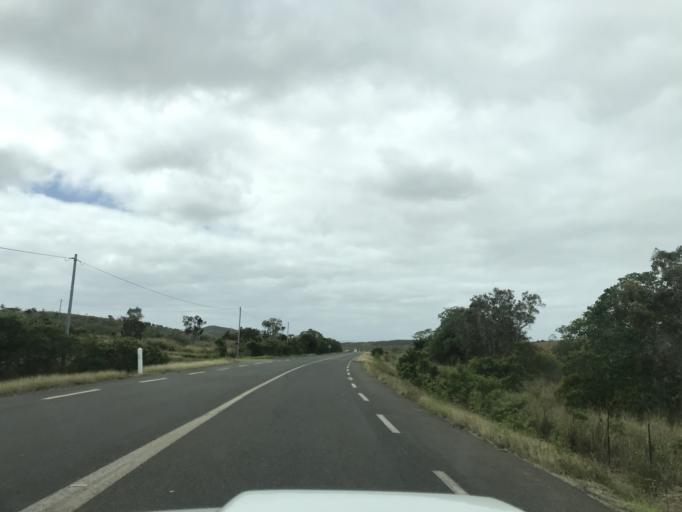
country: NC
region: South Province
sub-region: Bourail
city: Bourail
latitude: -21.7068
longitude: 165.6026
